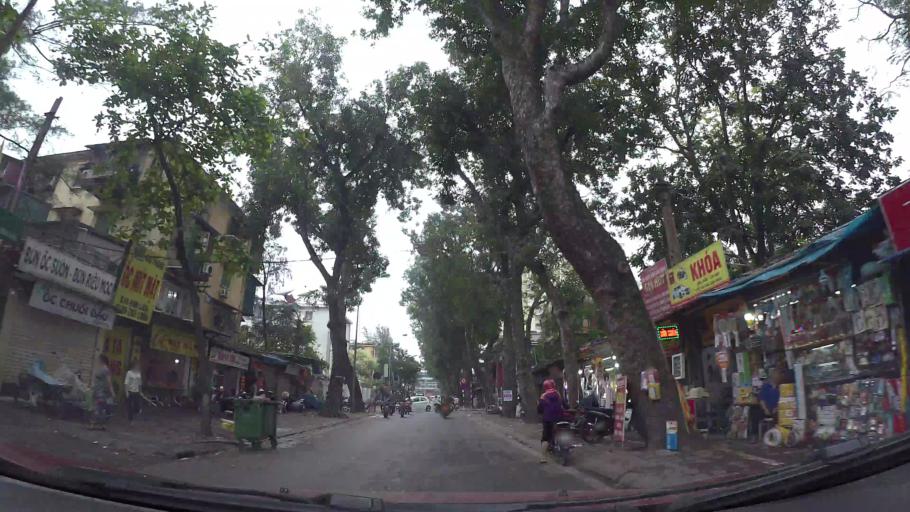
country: VN
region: Ha Noi
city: Dong Da
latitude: 21.0070
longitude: 105.8352
